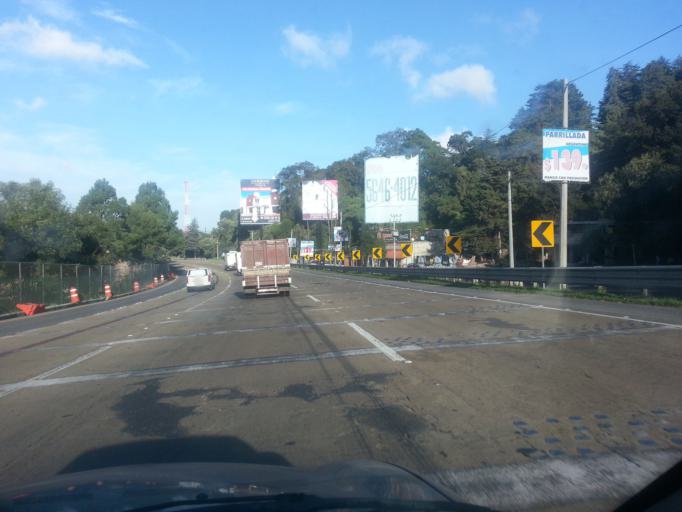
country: MX
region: Morelos
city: San Jeronimo Acazulco
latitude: 19.2924
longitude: -99.4297
